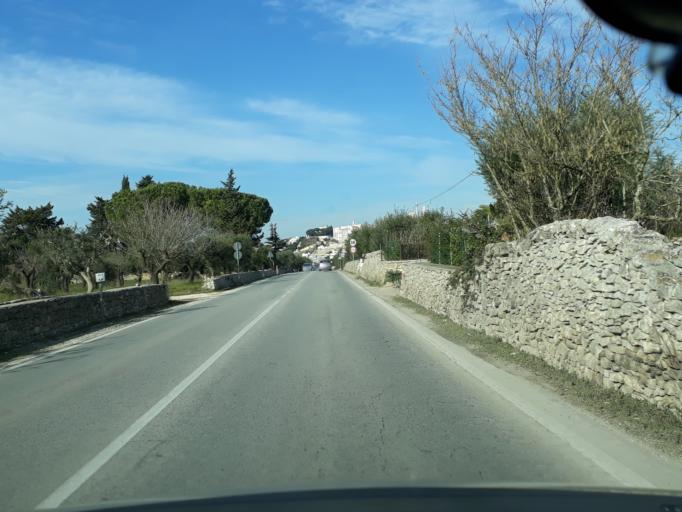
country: IT
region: Apulia
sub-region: Provincia di Bari
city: Locorotondo
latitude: 40.7424
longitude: 17.3323
